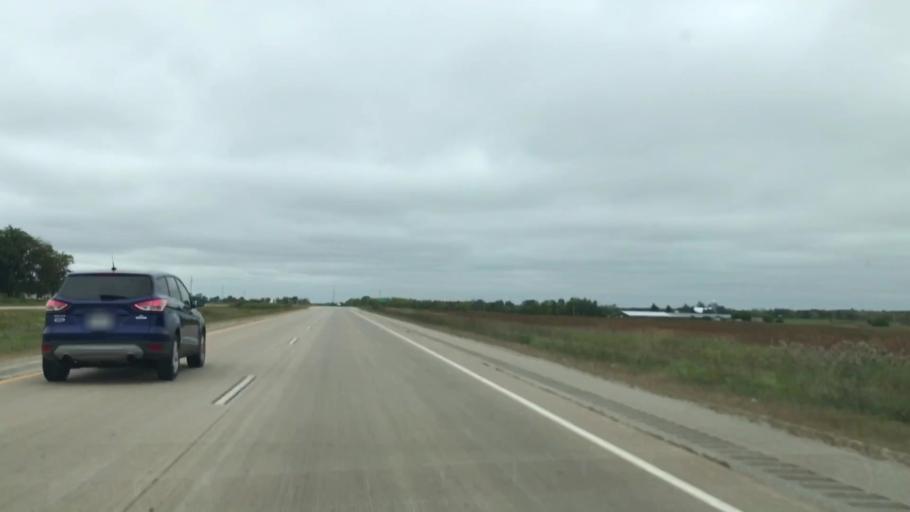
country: US
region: Wisconsin
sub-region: Marinette County
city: Peshtigo
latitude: 45.0232
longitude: -87.8341
